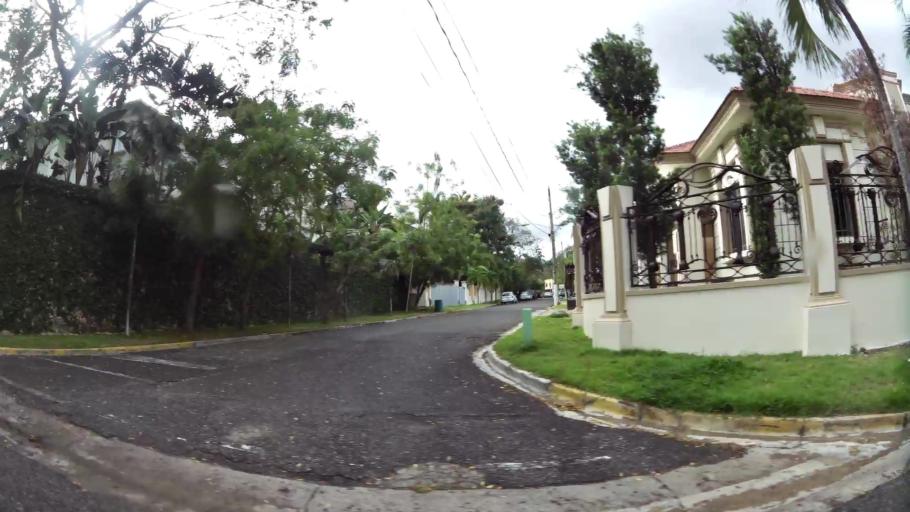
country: DO
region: Nacional
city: La Agustina
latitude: 18.5102
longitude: -69.9472
